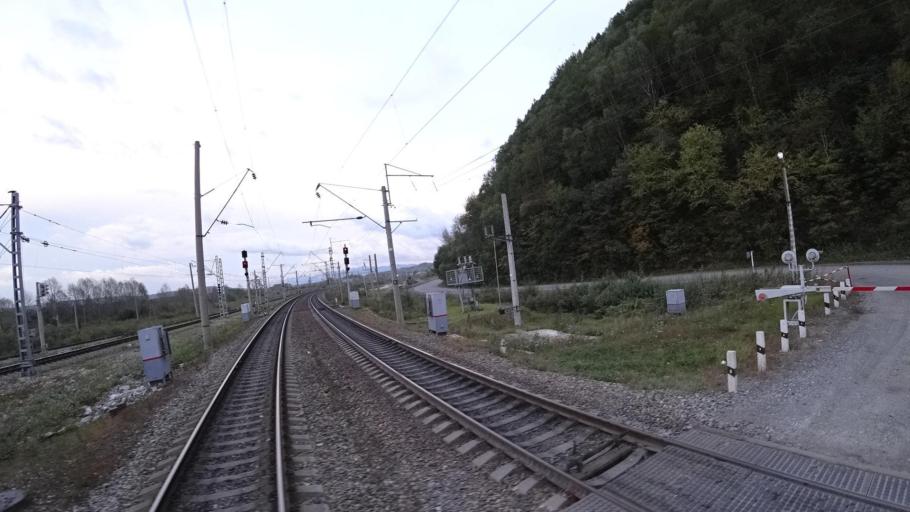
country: RU
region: Jewish Autonomous Oblast
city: Izvestkovyy
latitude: 48.9916
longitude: 131.5375
